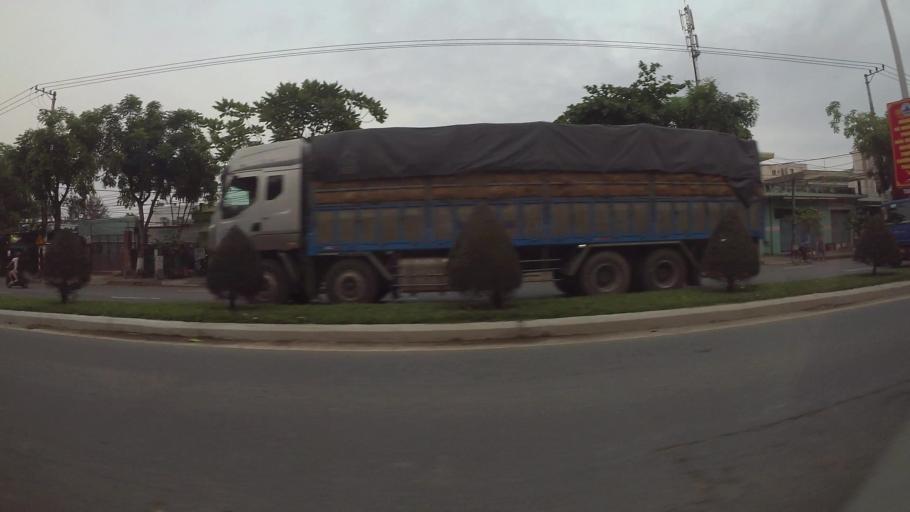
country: VN
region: Da Nang
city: Lien Chieu
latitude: 16.1082
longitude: 108.1311
